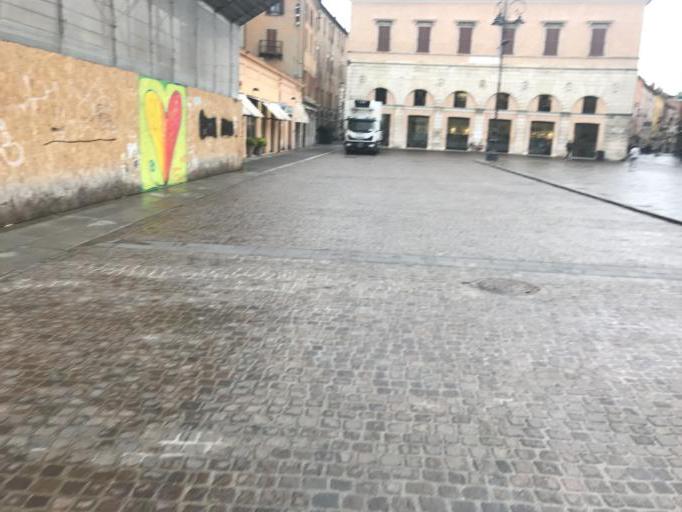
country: IT
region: Emilia-Romagna
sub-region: Provincia di Ferrara
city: Ferrara
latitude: 44.8352
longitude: 11.6206
